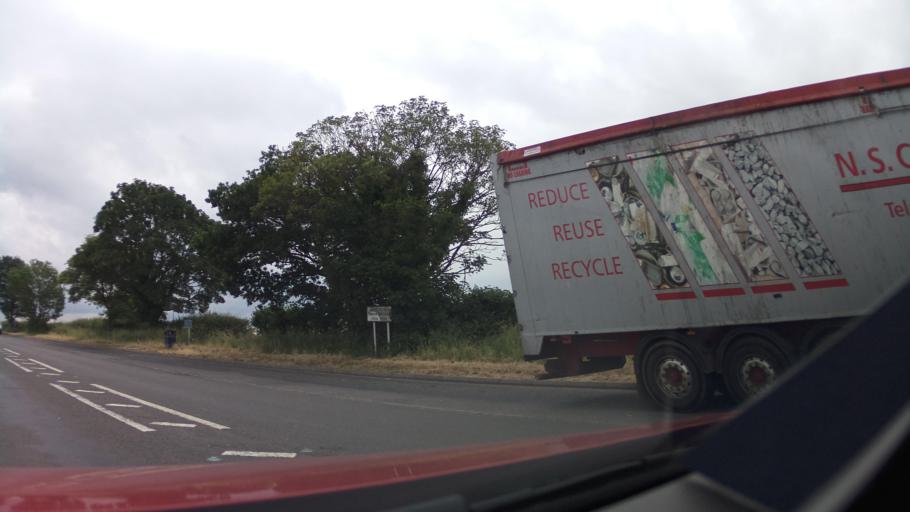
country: GB
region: England
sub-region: Staffordshire
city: Penkridge
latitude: 52.7407
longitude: -2.1091
